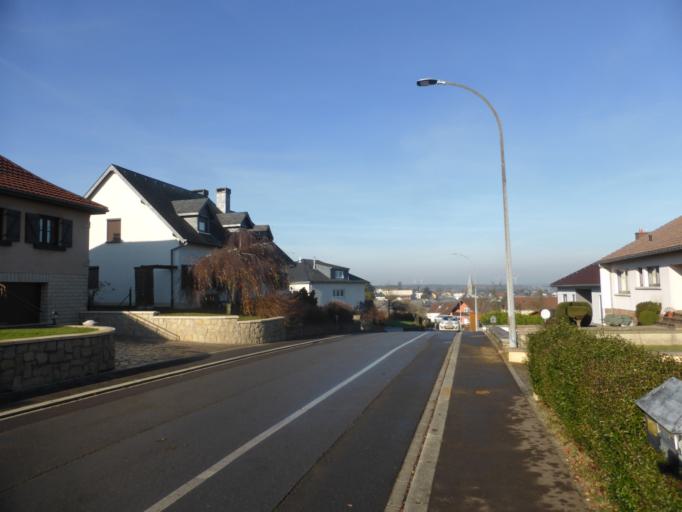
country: LU
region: Luxembourg
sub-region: Canton de Capellen
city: Clemency
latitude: 49.5941
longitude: 5.8750
